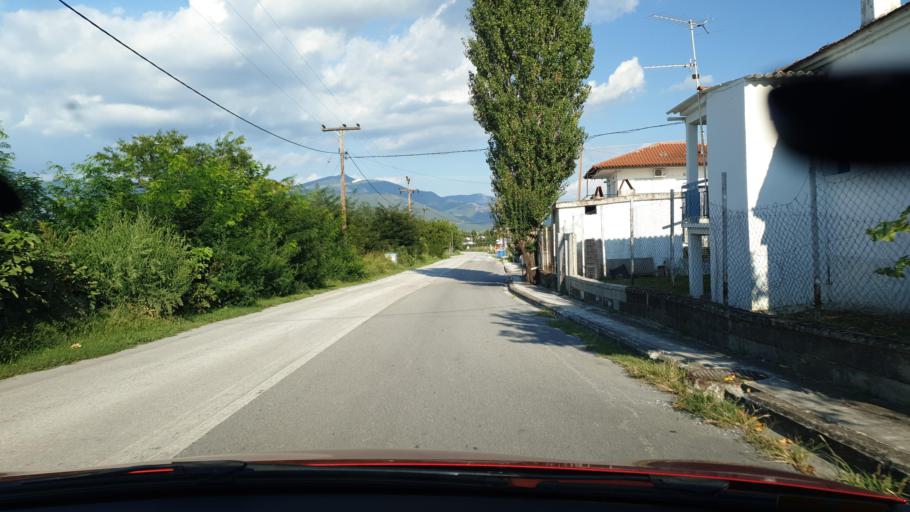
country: GR
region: Central Macedonia
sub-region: Nomos Thessalonikis
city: Souroti
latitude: 40.4743
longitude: 23.0932
